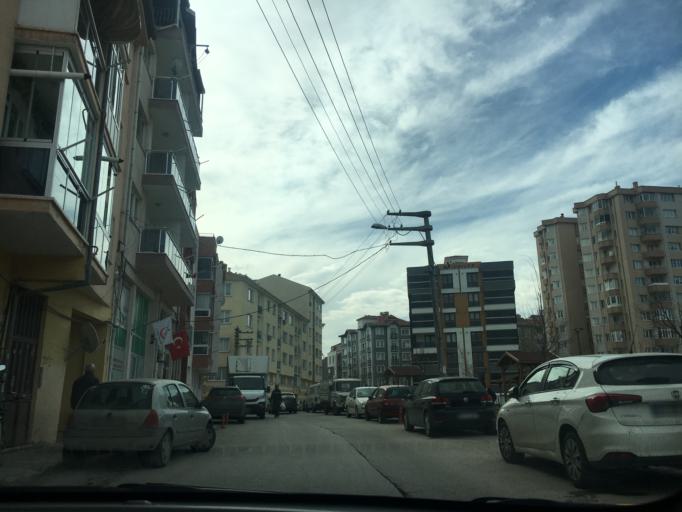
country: TR
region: Eskisehir
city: Eskisehir
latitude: 39.7741
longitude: 30.5042
